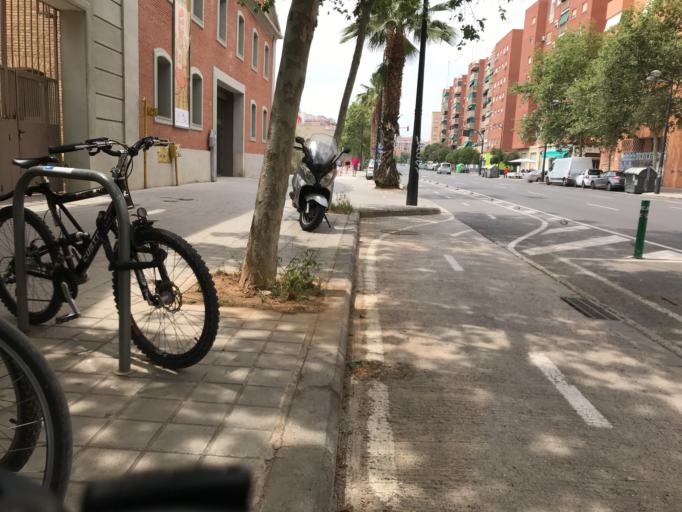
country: ES
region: Valencia
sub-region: Provincia de Valencia
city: Valencia
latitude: 39.4589
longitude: -0.3380
